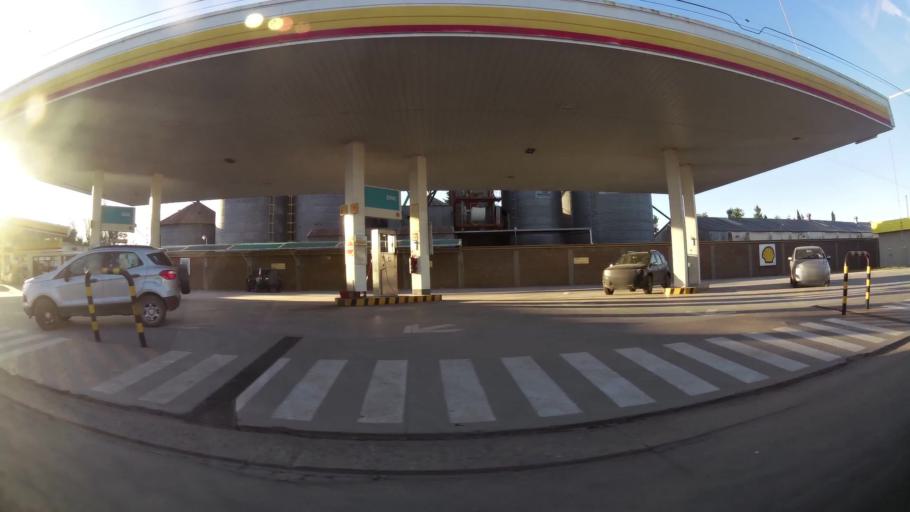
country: AR
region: Cordoba
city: Pozo del Molle
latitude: -32.0222
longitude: -62.9235
